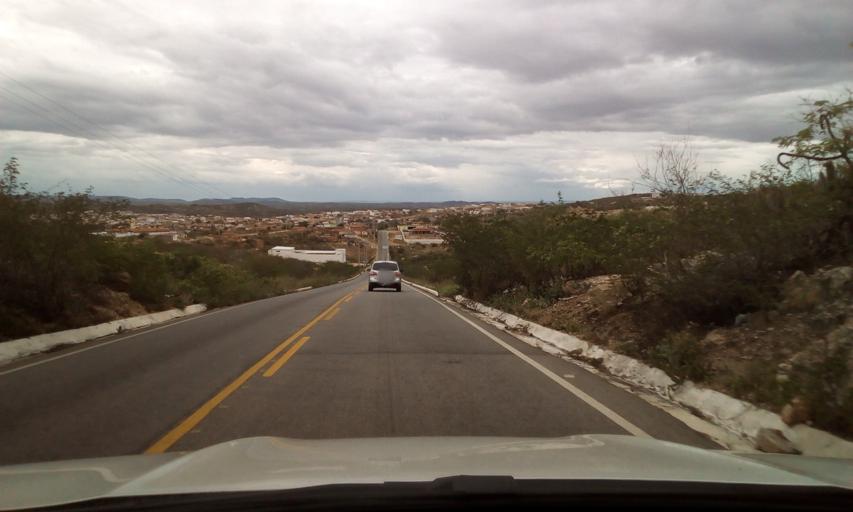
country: BR
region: Paraiba
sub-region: Picui
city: Picui
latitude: -6.5202
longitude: -36.3307
